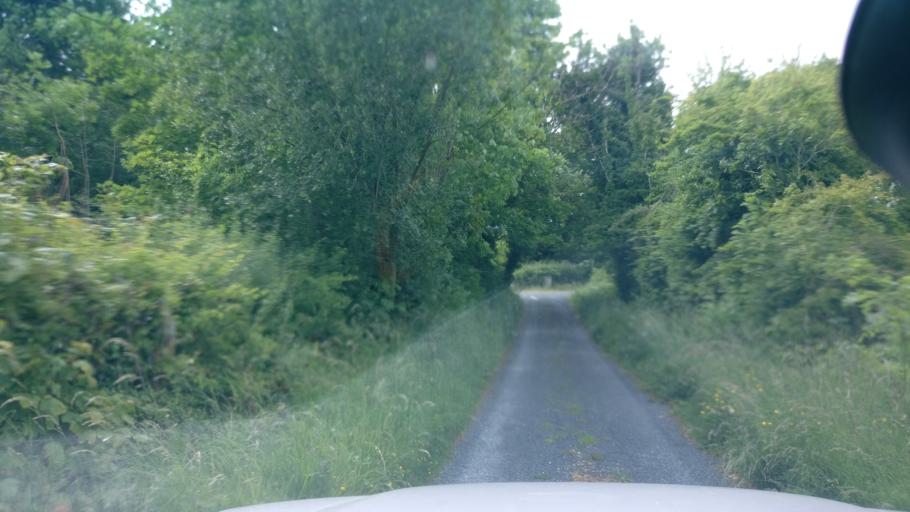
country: IE
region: Connaught
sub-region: County Galway
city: Ballinasloe
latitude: 53.2818
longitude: -8.3385
